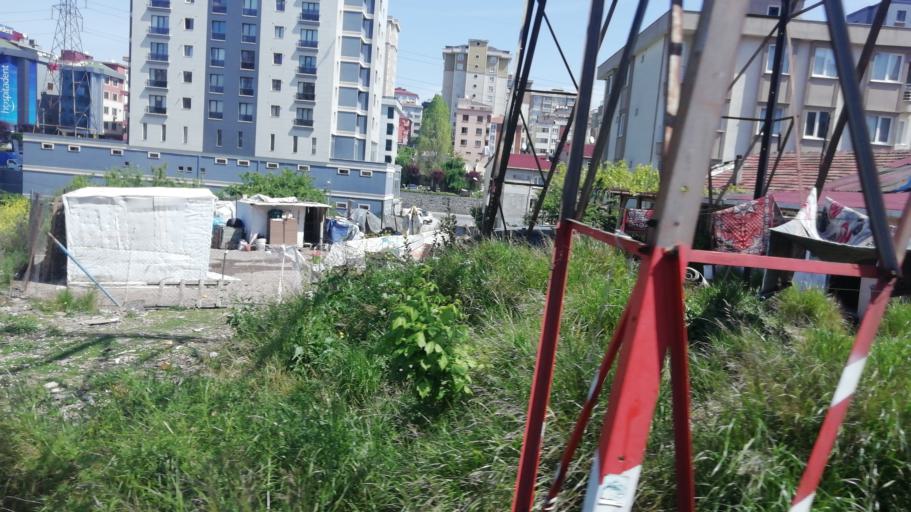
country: TR
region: Istanbul
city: Umraniye
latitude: 41.0007
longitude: 29.1423
